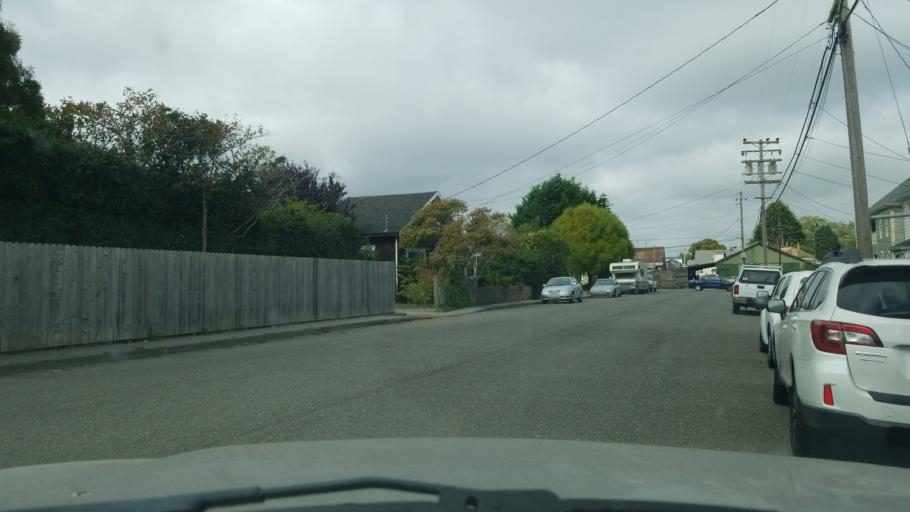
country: US
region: California
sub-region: Humboldt County
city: Ferndale
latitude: 40.5772
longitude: -124.2598
